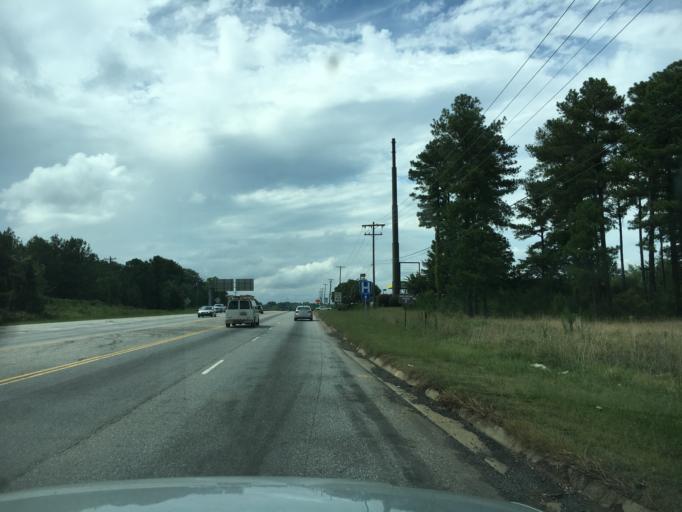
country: US
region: South Carolina
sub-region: Spartanburg County
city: Duncan
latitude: 34.8940
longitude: -82.1615
